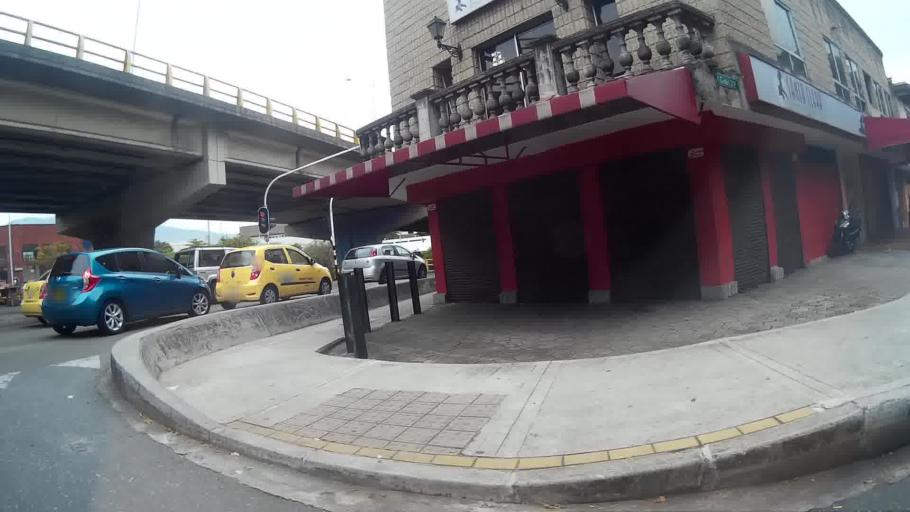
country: CO
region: Antioquia
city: Medellin
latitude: 6.2387
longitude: -75.5902
